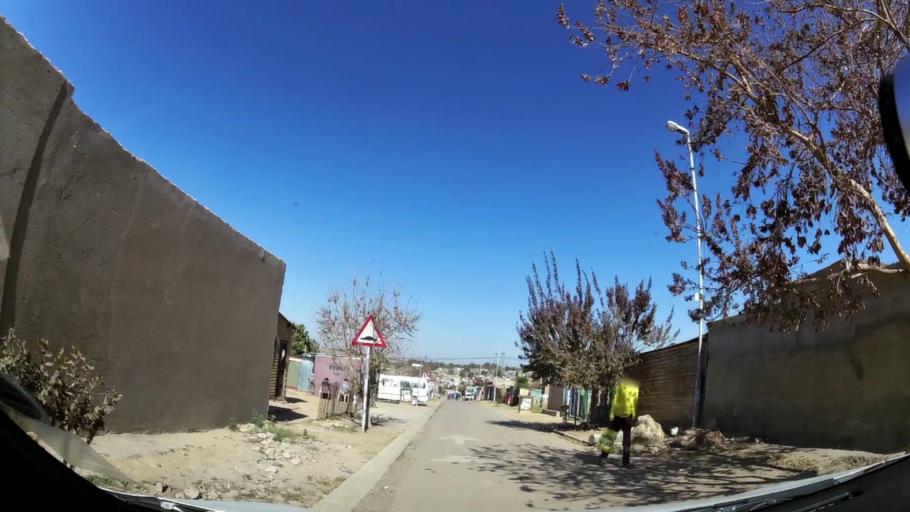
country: ZA
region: Gauteng
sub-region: City of Johannesburg Metropolitan Municipality
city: Diepsloot
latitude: -25.9163
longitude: 28.0888
